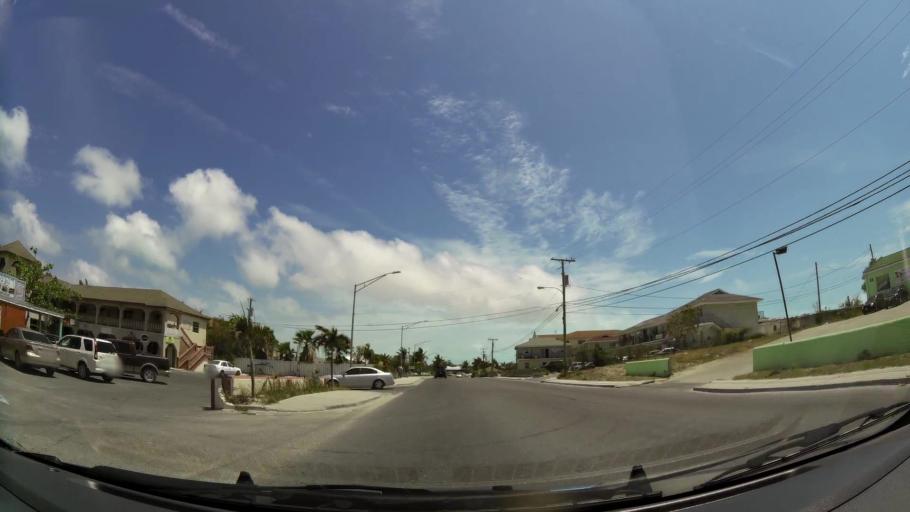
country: BS
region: Mayaguana
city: Abraham's Bay
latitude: 21.7773
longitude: -72.2597
